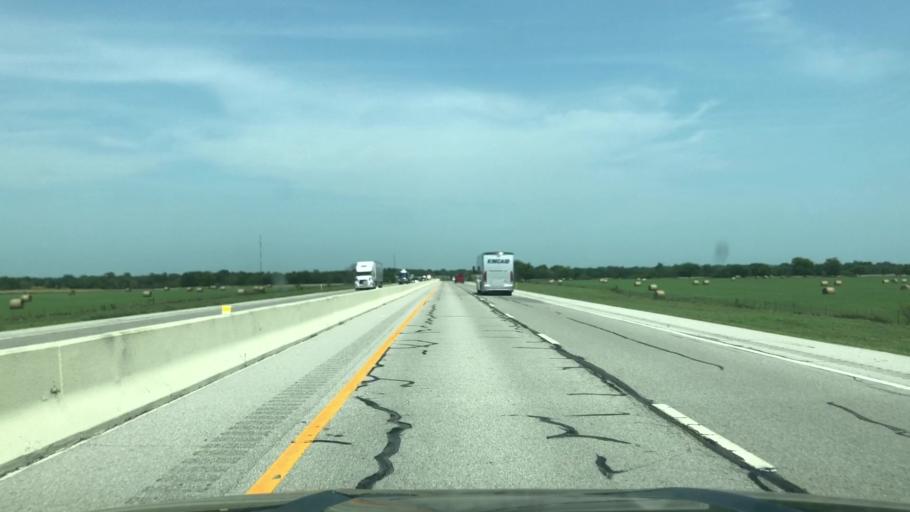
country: US
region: Oklahoma
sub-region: Rogers County
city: Chelsea
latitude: 36.4965
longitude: -95.2893
